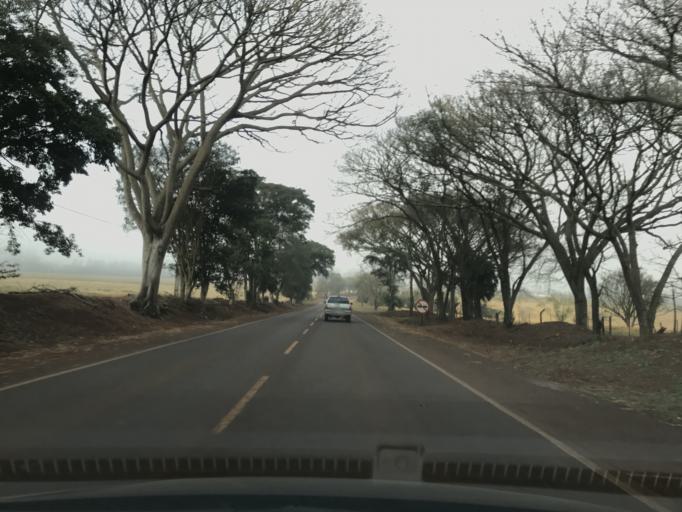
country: BR
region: Parana
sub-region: Toledo
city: Toledo
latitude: -24.7022
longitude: -53.6979
